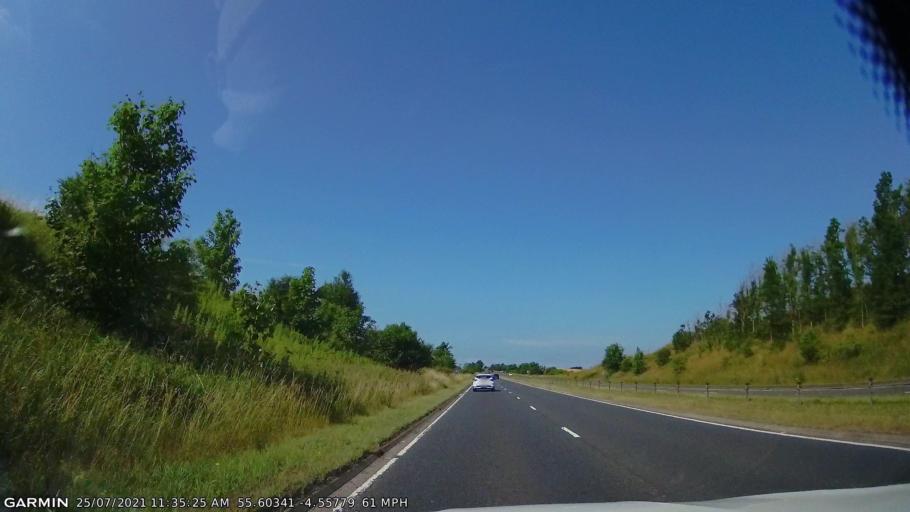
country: GB
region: Scotland
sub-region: East Ayrshire
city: Crosshouse
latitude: 55.6034
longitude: -4.5578
